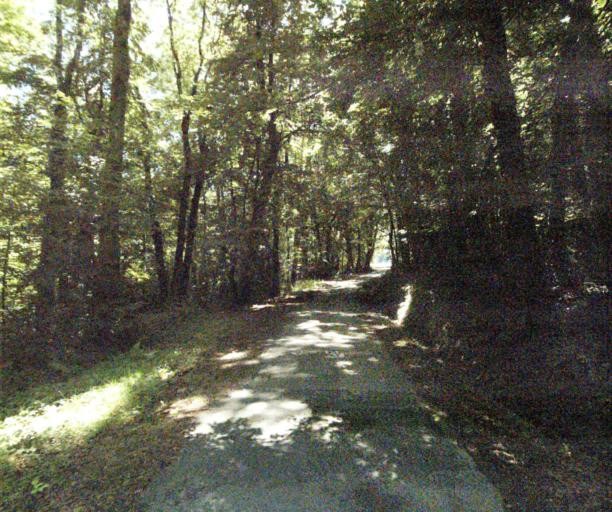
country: FR
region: Midi-Pyrenees
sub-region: Departement du Tarn
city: Dourgne
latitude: 43.4321
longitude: 2.1591
